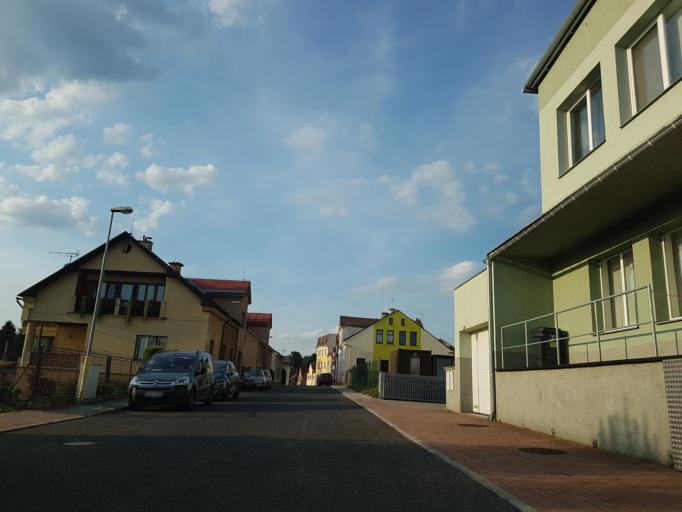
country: CZ
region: Liberecky
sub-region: Okres Jablonec nad Nisou
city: Jablonec nad Nisou
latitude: 50.7262
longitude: 15.1787
